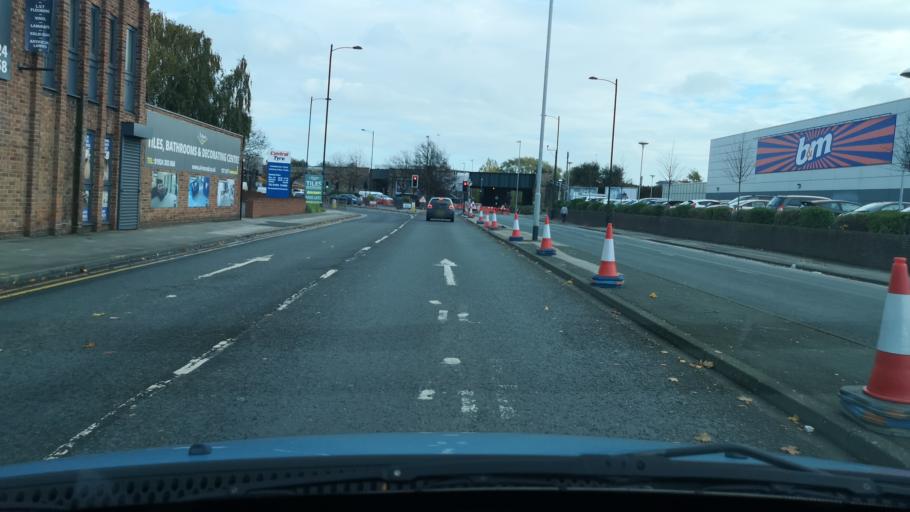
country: GB
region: England
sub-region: City and Borough of Wakefield
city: Wakefield
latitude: 53.6780
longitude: -1.4948
